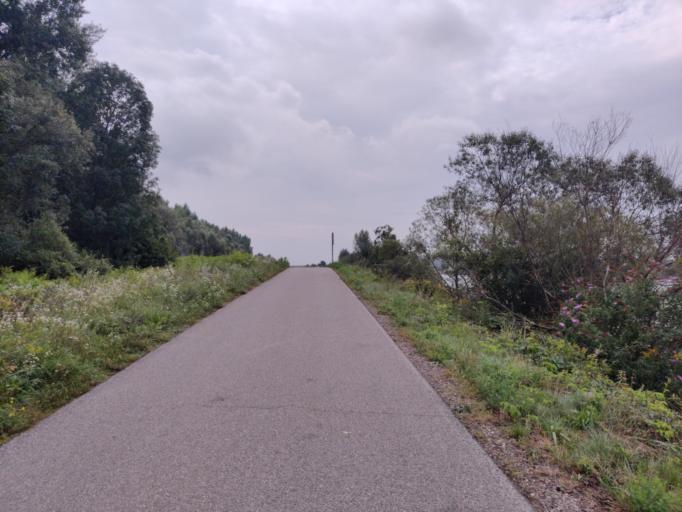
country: AT
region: Upper Austria
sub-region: Politischer Bezirk Urfahr-Umgebung
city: Steyregg
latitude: 48.2819
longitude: 14.3491
